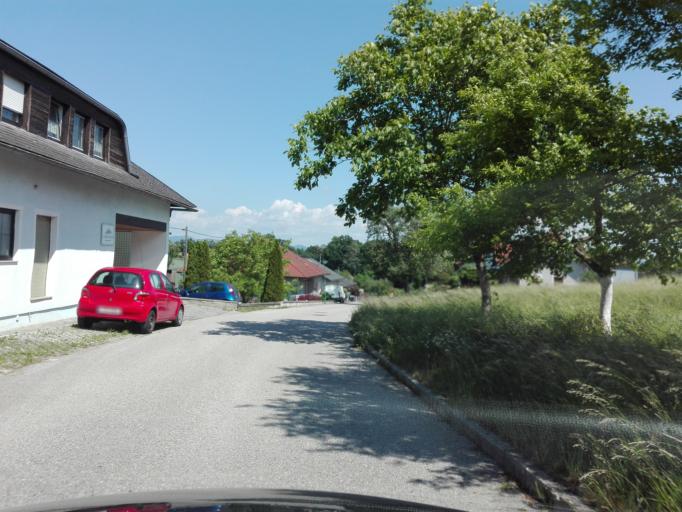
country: AT
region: Upper Austria
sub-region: Politischer Bezirk Linz-Land
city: Enns
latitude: 48.2805
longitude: 14.4768
